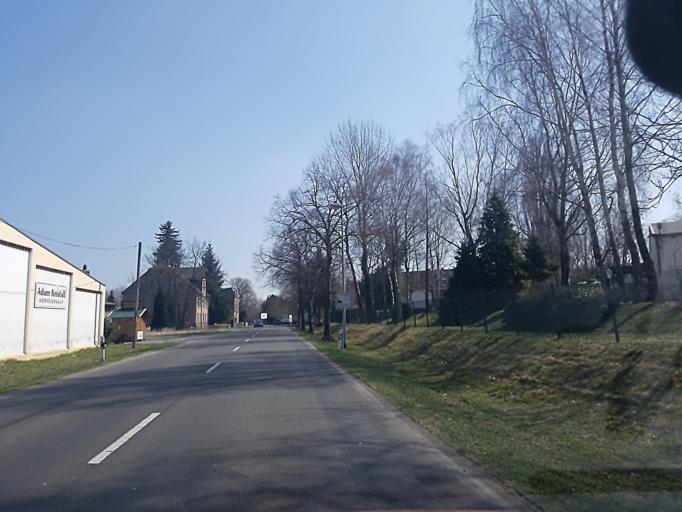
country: DE
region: Brandenburg
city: Tschernitz
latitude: 51.6258
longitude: 14.5825
